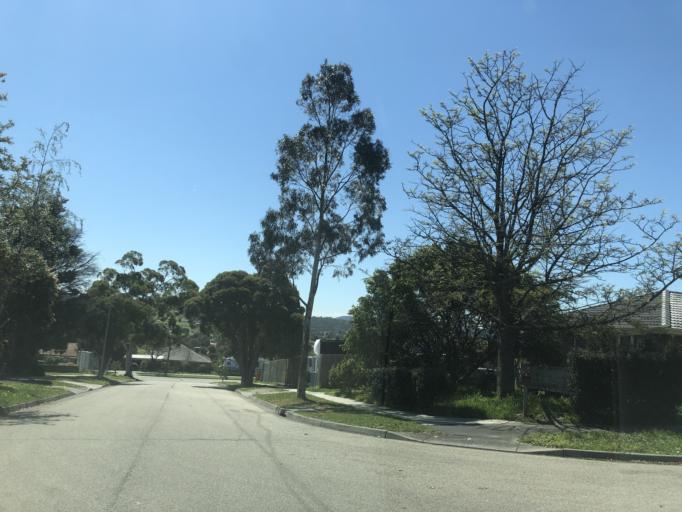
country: AU
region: Victoria
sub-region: Casey
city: Endeavour Hills
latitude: -37.9748
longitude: 145.2630
